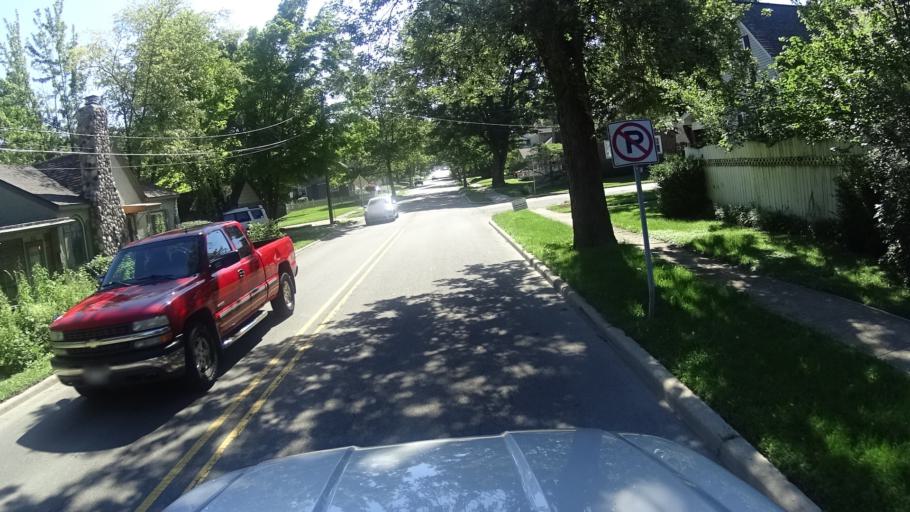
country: US
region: Indiana
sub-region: Madison County
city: Pendleton
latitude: 40.0024
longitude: -85.7523
